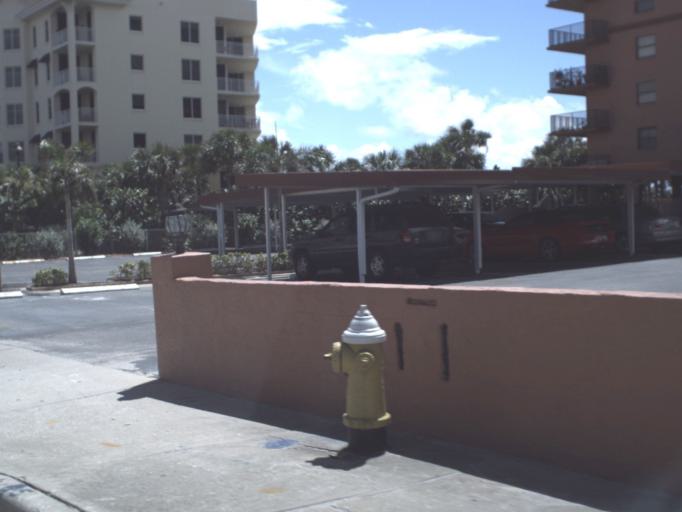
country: US
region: Florida
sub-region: Pinellas County
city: Redington Beach
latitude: 27.8037
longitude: -82.8047
